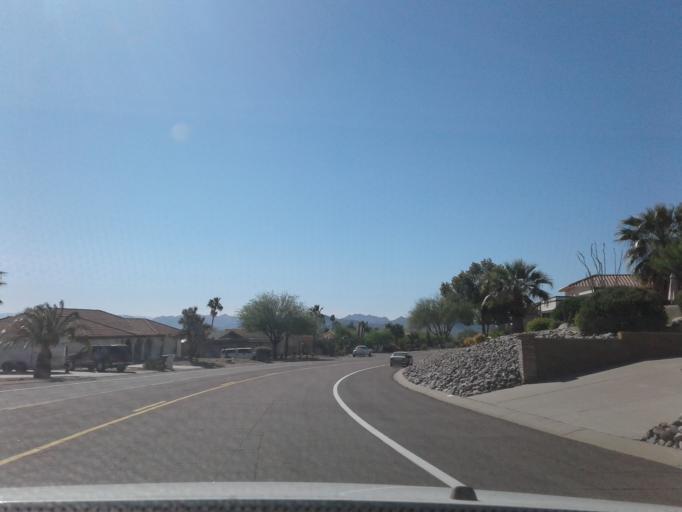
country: US
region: Arizona
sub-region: Maricopa County
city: Fountain Hills
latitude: 33.5939
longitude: -111.7520
